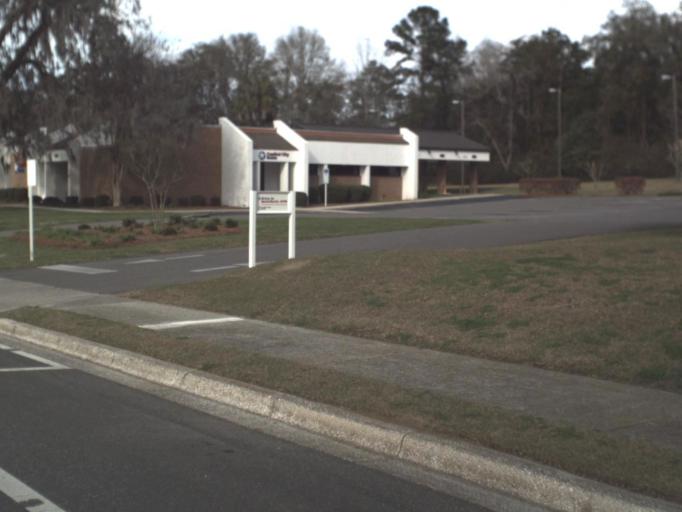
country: US
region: Florida
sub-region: Jefferson County
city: Monticello
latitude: 30.5386
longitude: -83.8702
